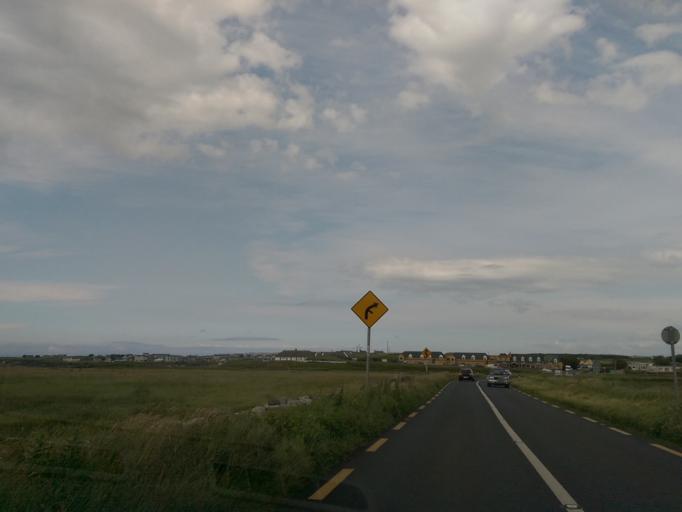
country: IE
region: Munster
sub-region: An Clar
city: Kilrush
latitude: 52.8347
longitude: -9.4306
